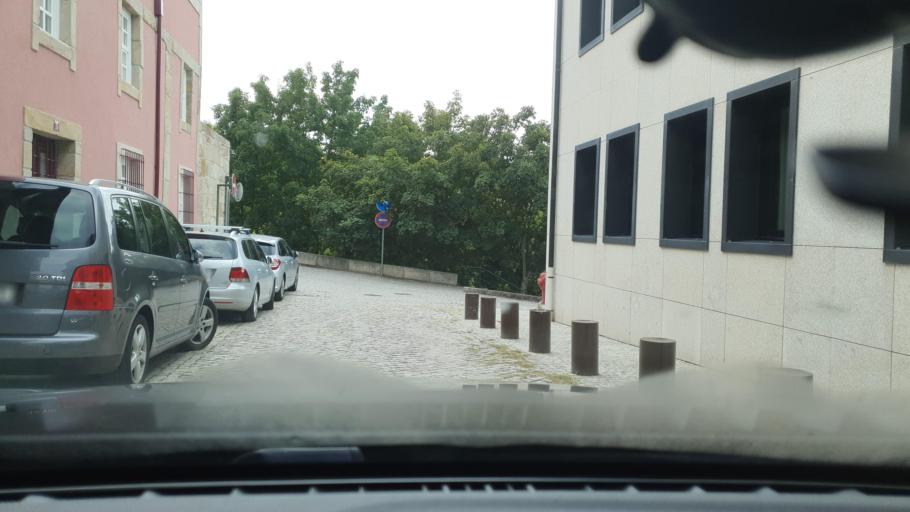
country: PT
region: Vila Real
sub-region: Chaves
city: Chaves
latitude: 41.7405
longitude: -7.4725
